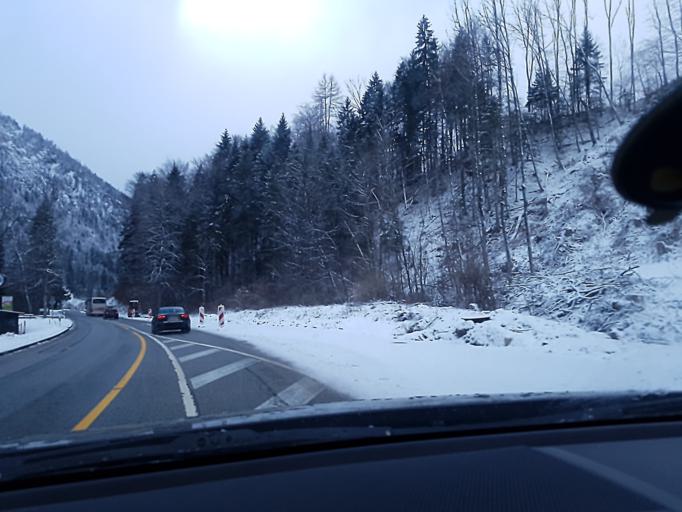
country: DE
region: Bavaria
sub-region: Upper Bavaria
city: Marktschellenberg
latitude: 47.6569
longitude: 13.0412
